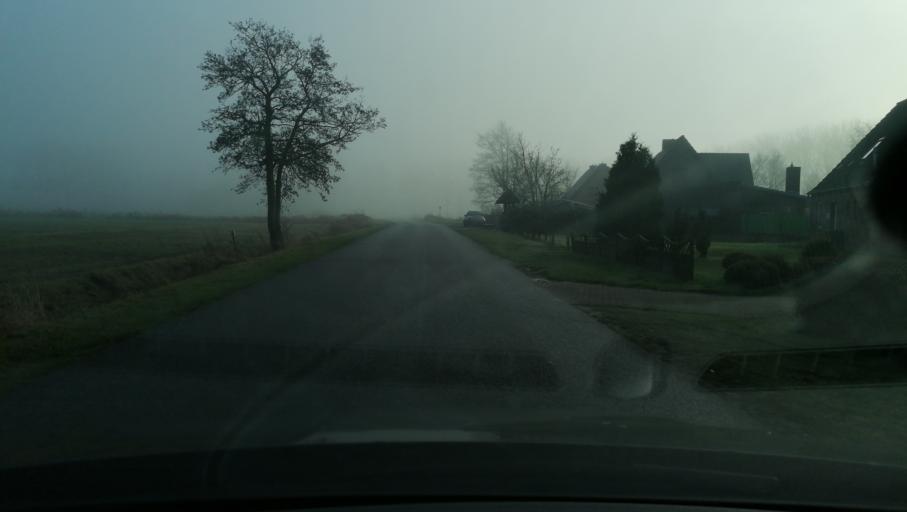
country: DE
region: Schleswig-Holstein
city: Epenwohrden
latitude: 54.1022
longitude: 9.0480
